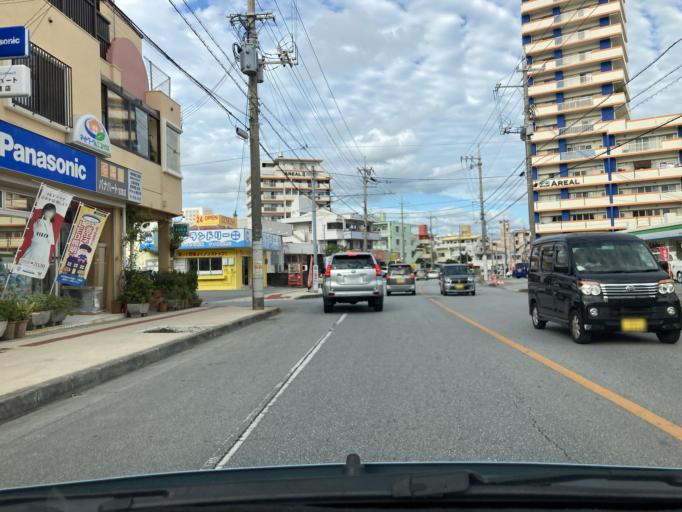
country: JP
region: Okinawa
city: Okinawa
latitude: 26.3407
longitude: 127.8222
